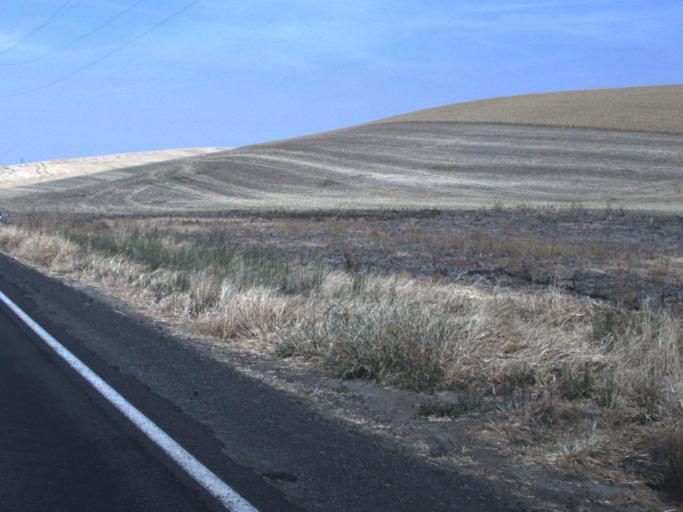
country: US
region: Washington
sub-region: Whitman County
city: Colfax
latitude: 47.0833
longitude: -117.1576
